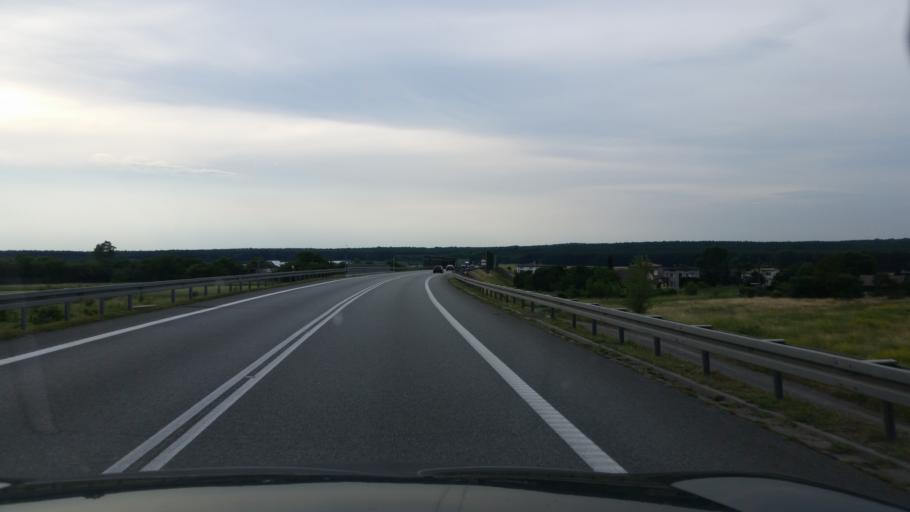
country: PL
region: Silesian Voivodeship
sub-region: Powiat bedzinski
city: Mierzecice
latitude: 50.4444
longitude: 19.1410
